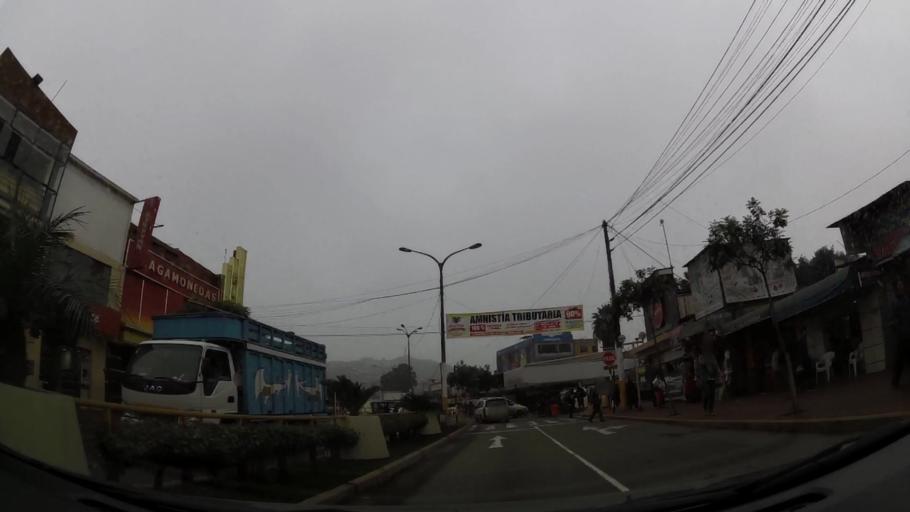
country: PE
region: Lima
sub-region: Lima
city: Carabayllo
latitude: -11.8656
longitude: -77.0765
